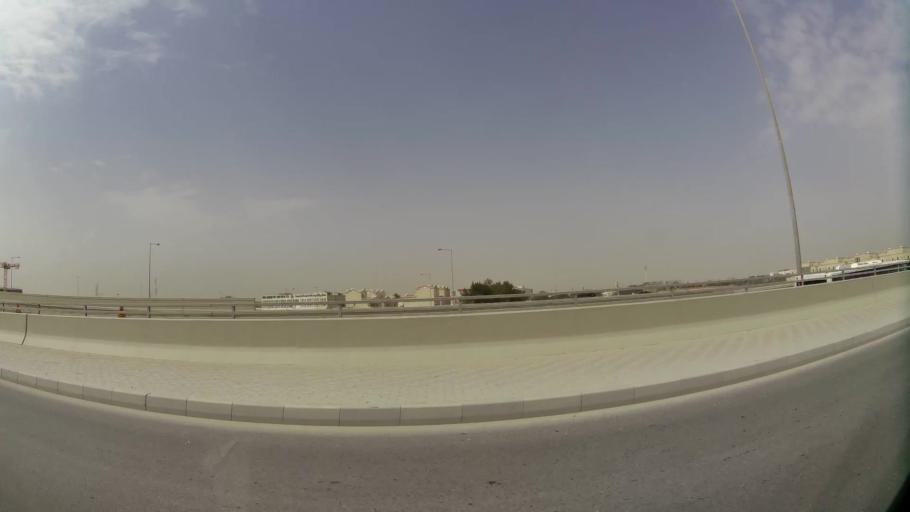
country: QA
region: Baladiyat ar Rayyan
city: Ar Rayyan
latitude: 25.2986
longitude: 51.4747
